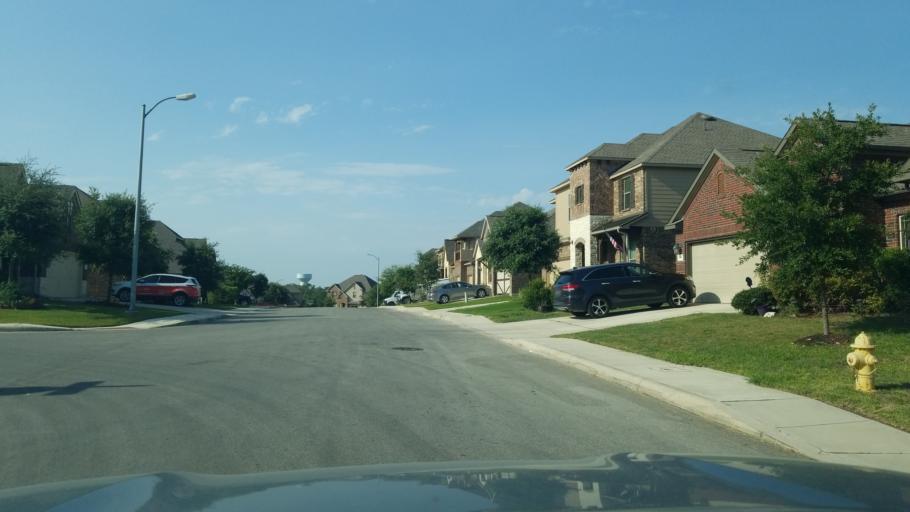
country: US
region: Texas
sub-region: Medina County
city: La Coste
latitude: 29.4388
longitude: -98.7534
